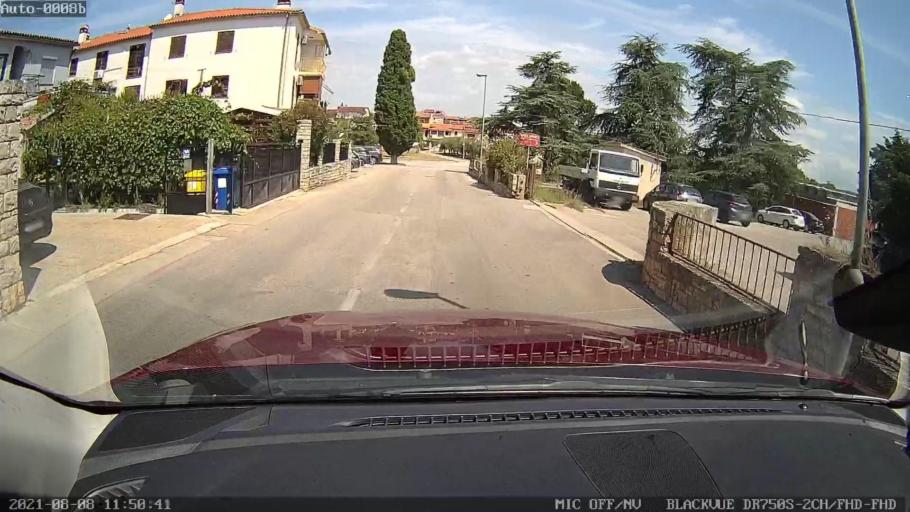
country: HR
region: Istarska
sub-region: Grad Rovinj
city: Rovinj
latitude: 45.0812
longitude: 13.6487
